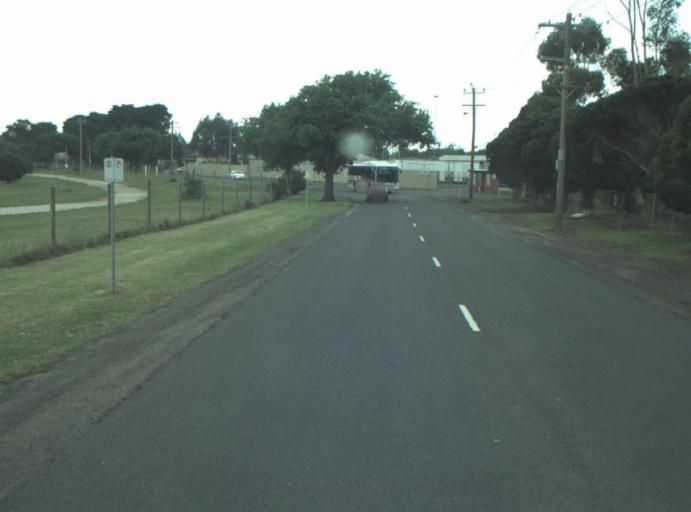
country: AU
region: Victoria
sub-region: Greater Geelong
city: Breakwater
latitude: -38.1737
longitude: 144.3713
